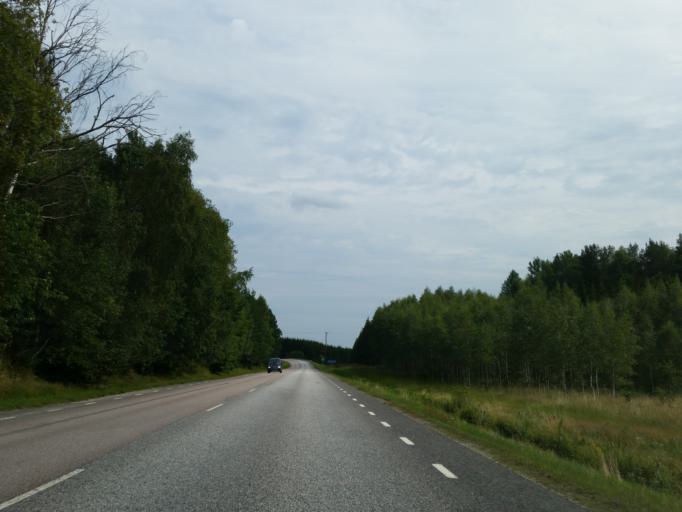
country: SE
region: Soedermanland
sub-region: Strangnas Kommun
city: Mariefred
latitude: 59.2229
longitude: 17.2248
